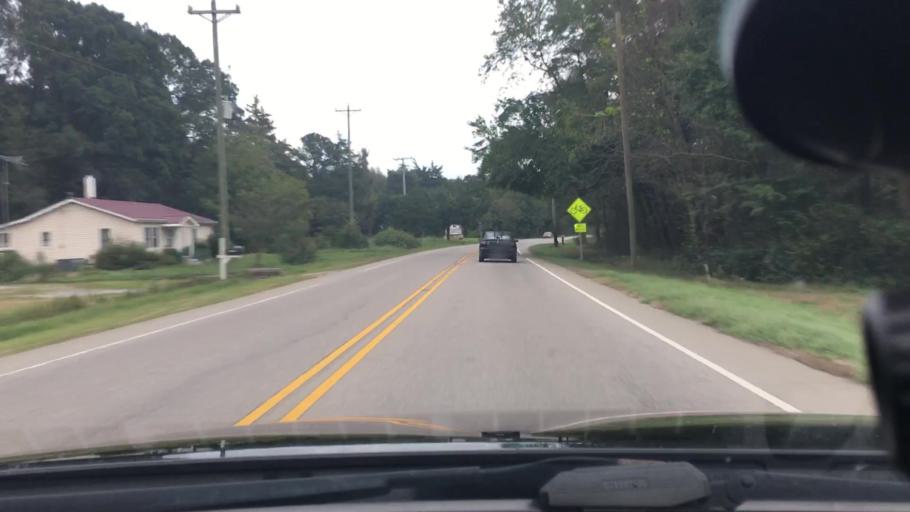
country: US
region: North Carolina
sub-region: Moore County
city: Robbins
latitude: 35.4033
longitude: -79.5614
